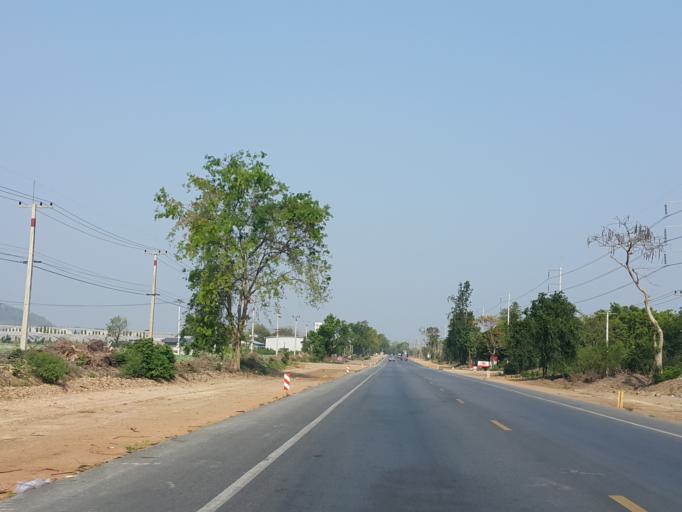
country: TH
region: Kanchanaburi
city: Sai Yok
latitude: 14.0888
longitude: 99.3243
